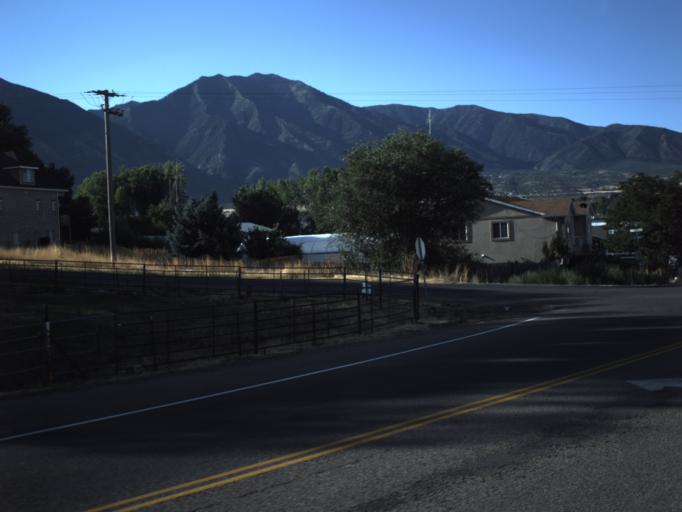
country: US
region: Utah
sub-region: Utah County
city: Salem
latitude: 40.0715
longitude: -111.6629
